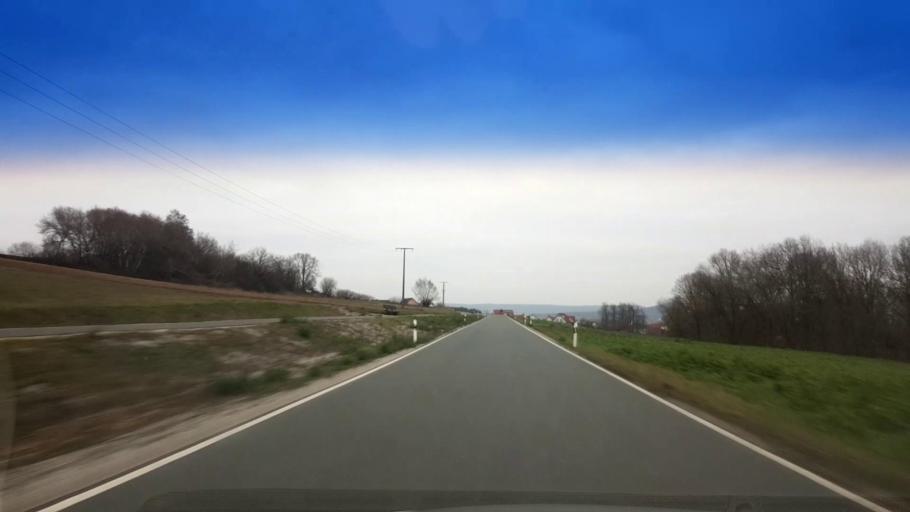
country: DE
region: Bavaria
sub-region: Upper Franconia
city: Hallerndorf
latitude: 49.7689
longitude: 10.9946
